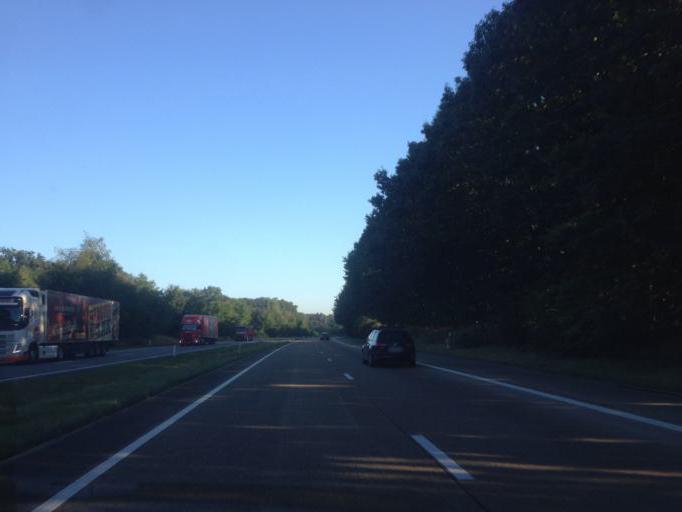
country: BE
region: Flanders
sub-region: Provincie Limburg
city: Overpelt
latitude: 51.1814
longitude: 5.3938
